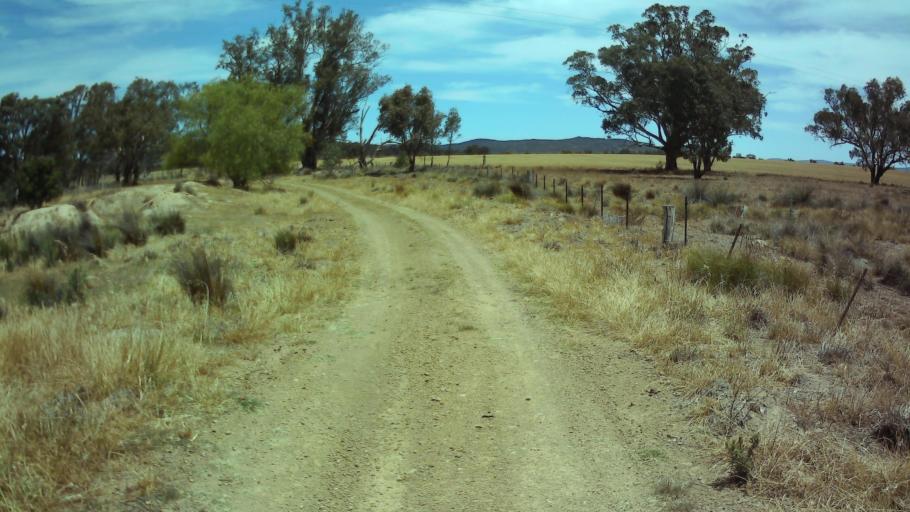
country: AU
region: New South Wales
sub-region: Weddin
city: Grenfell
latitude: -33.7605
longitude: 148.1453
